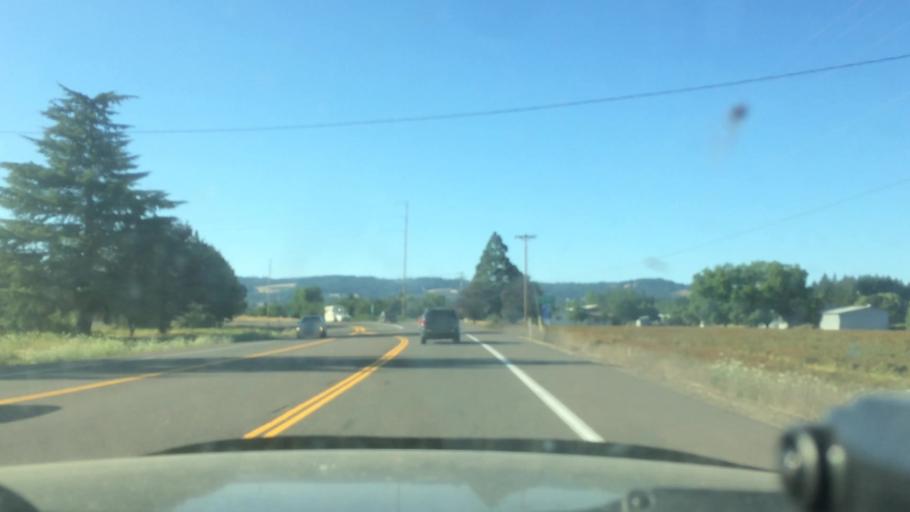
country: US
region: Oregon
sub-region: Yamhill County
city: Newberg
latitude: 45.2847
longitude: -122.9452
